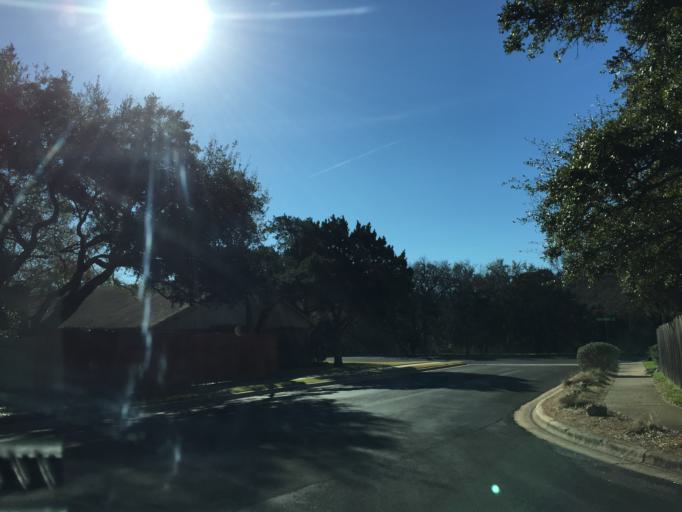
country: US
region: Texas
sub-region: Williamson County
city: Jollyville
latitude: 30.4040
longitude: -97.7302
